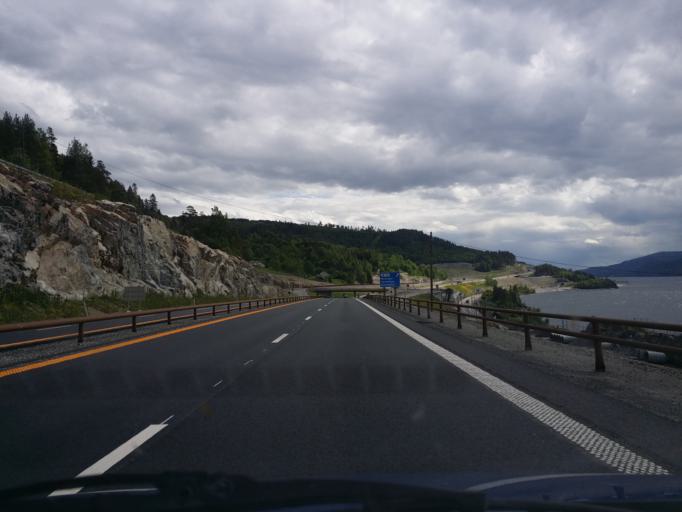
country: NO
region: Akershus
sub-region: Eidsvoll
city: Eidsvoll
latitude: 60.5188
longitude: 11.2427
